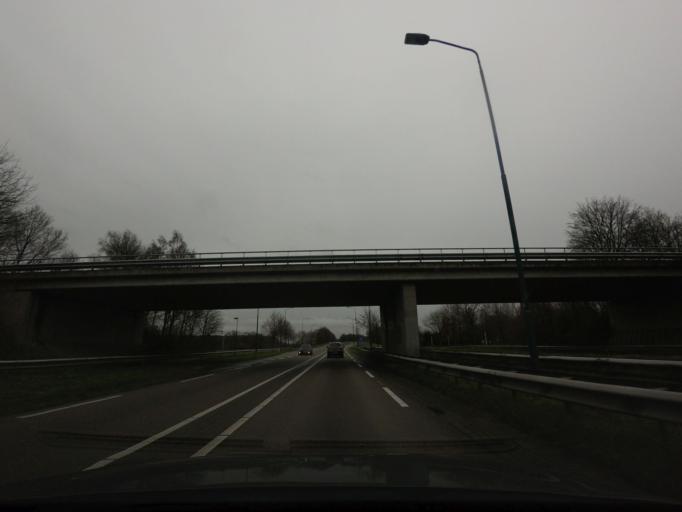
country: NL
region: North Brabant
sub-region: Gemeente Hilvarenbeek
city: Hilvarenbeek
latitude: 51.4894
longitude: 5.1471
